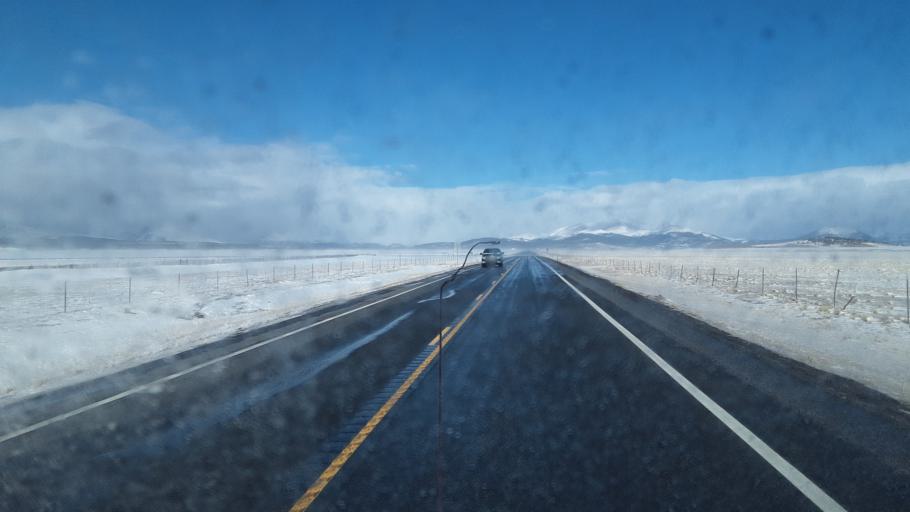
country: US
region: Colorado
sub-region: Park County
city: Fairplay
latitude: 39.1502
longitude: -105.9987
